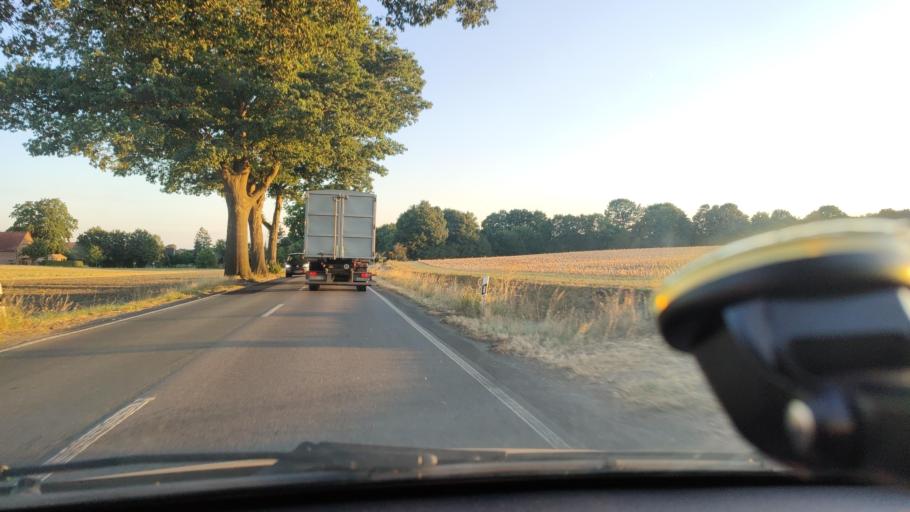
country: DE
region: North Rhine-Westphalia
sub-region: Regierungsbezirk Munster
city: Klein Reken
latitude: 51.7692
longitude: 6.9998
